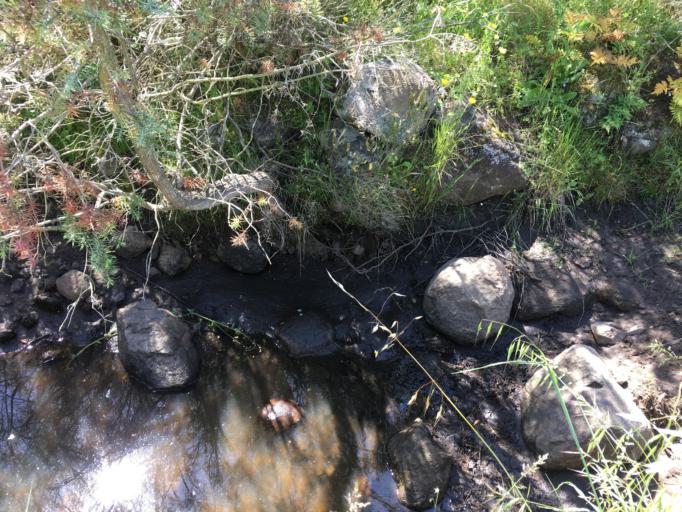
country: FR
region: Provence-Alpes-Cote d'Azur
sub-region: Departement des Alpes-Maritimes
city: Biot
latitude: 43.6408
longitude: 7.1030
